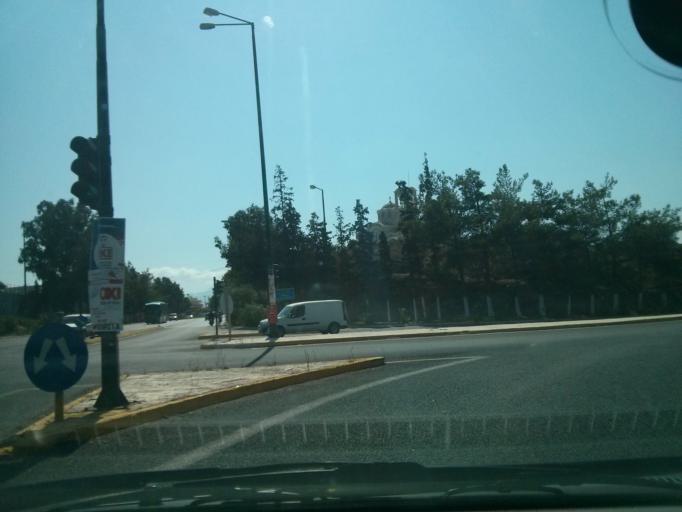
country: GR
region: Crete
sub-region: Nomos Lasithiou
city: Agios Nikolaos
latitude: 35.1998
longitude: 25.7062
